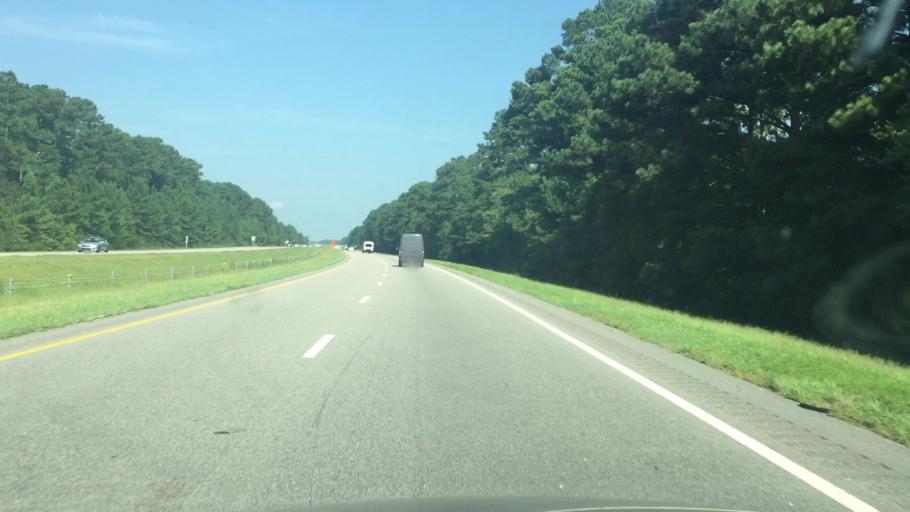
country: US
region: North Carolina
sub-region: Robeson County
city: Lumberton
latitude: 34.5724
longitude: -79.0343
